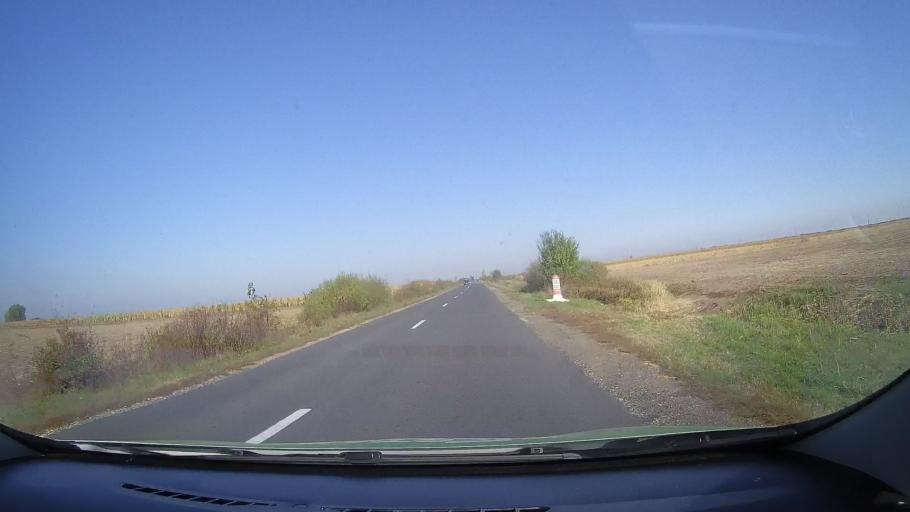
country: RO
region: Satu Mare
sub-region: Oras Tasnad
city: Tasnad
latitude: 47.5186
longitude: 22.5711
